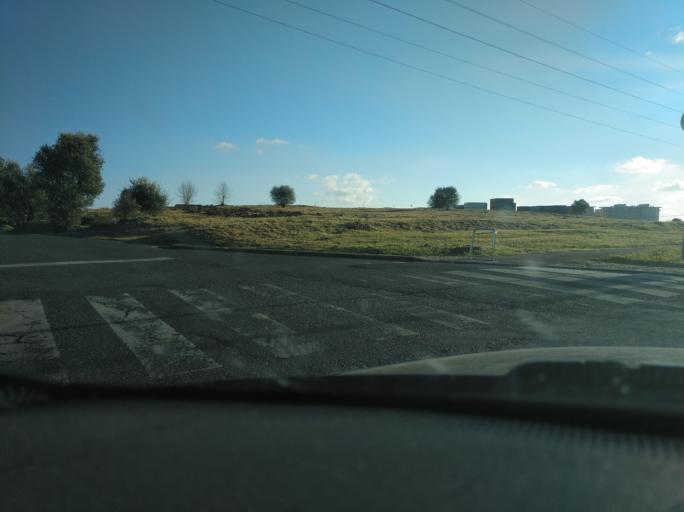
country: PT
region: Lisbon
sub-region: Odivelas
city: Pontinha
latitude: 38.7736
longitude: -9.1827
